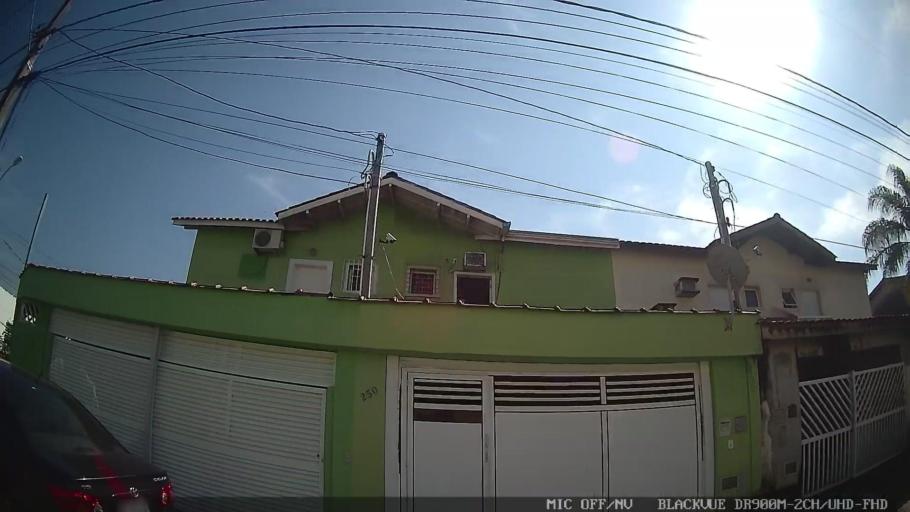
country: BR
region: Sao Paulo
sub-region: Guaruja
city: Guaruja
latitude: -24.0063
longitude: -46.2752
